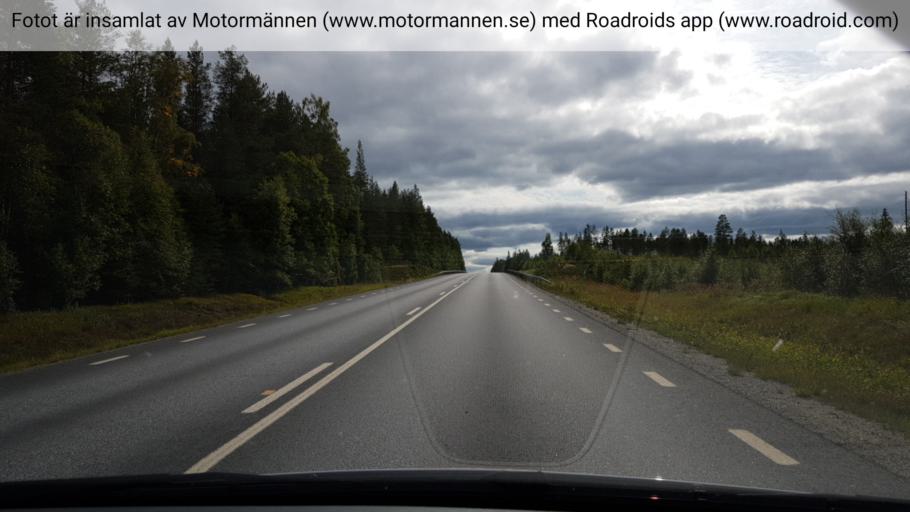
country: SE
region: Vaesterbotten
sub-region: Vannas Kommun
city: Vannasby
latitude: 64.0540
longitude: 19.9968
